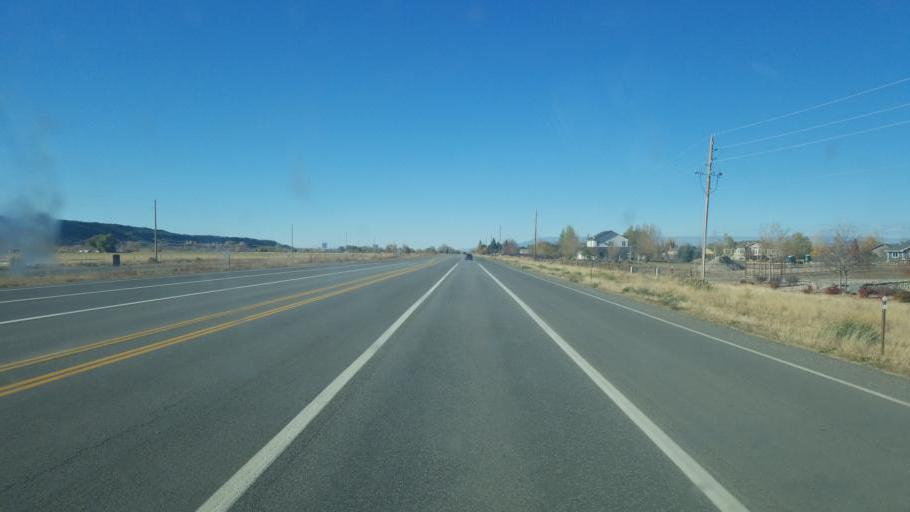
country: US
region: Colorado
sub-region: Montrose County
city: Montrose
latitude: 38.3781
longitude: -107.8187
